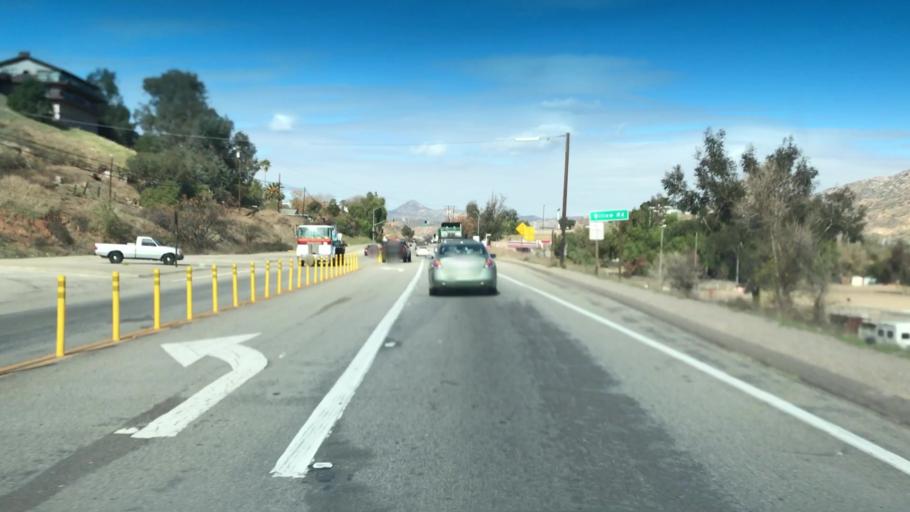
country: US
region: California
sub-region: San Diego County
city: Lakeside
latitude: 32.8714
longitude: -116.9236
